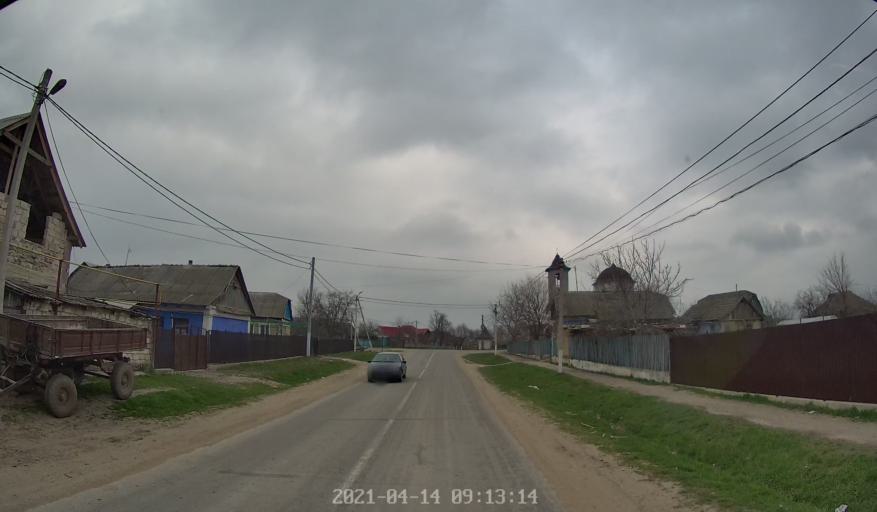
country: MD
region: Chisinau
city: Vadul lui Voda
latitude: 47.1015
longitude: 29.1119
